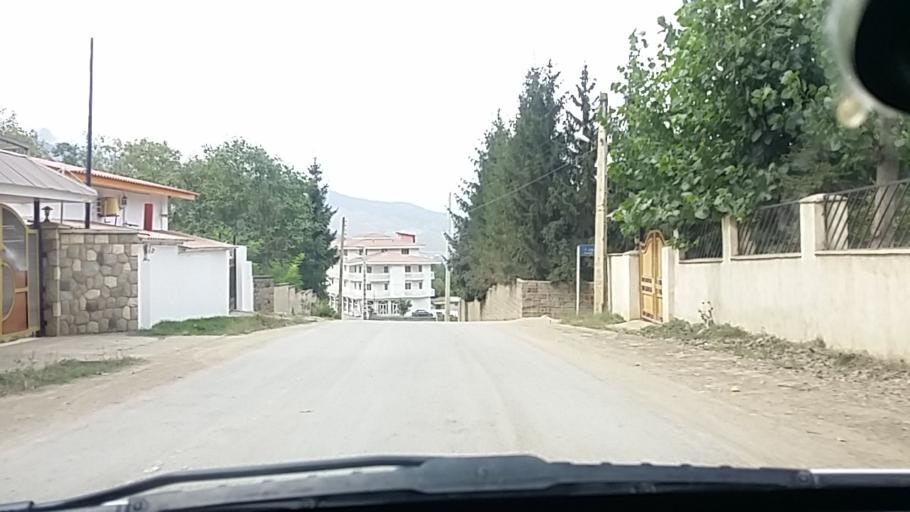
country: IR
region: Mazandaran
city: `Abbasabad
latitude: 36.4956
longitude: 51.1653
